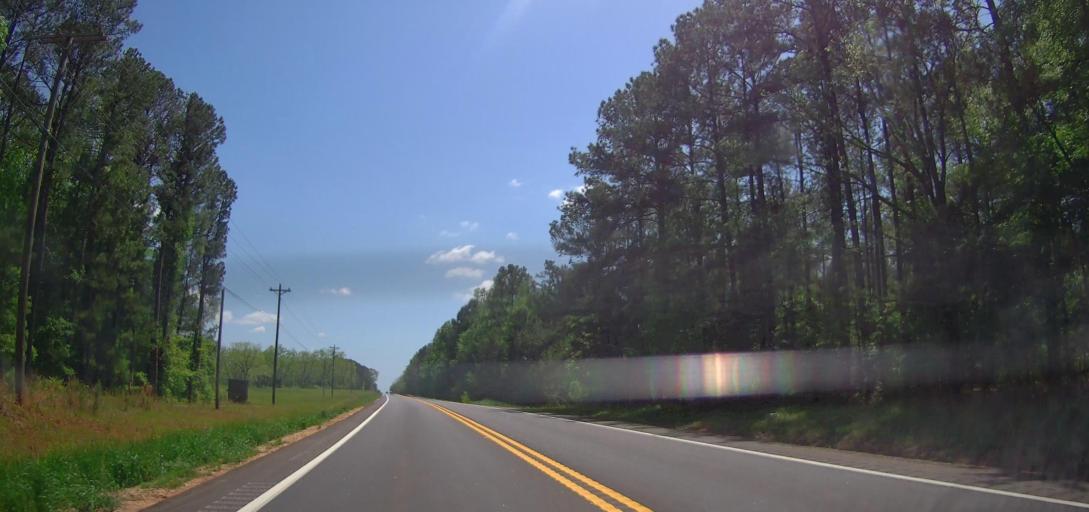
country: US
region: Georgia
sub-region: Putnam County
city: Eatonton
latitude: 33.2095
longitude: -83.4347
